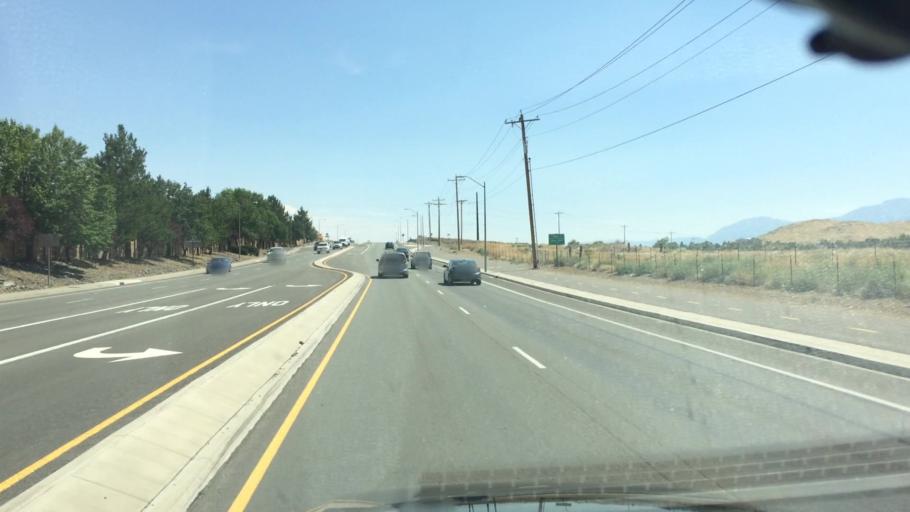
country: US
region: Nevada
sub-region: Washoe County
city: Sparks
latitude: 39.5756
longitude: -119.7242
